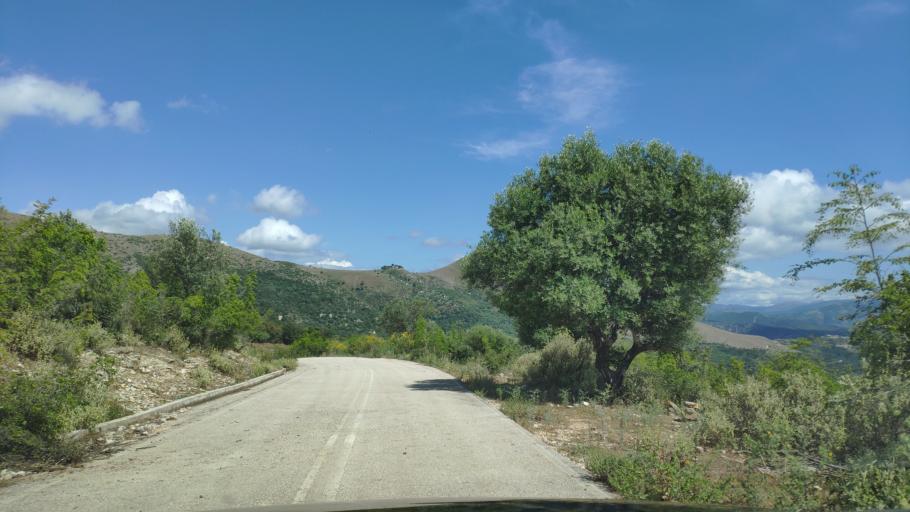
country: AL
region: Vlore
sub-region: Rrethi i Sarandes
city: Konispol
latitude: 39.6318
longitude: 20.2107
